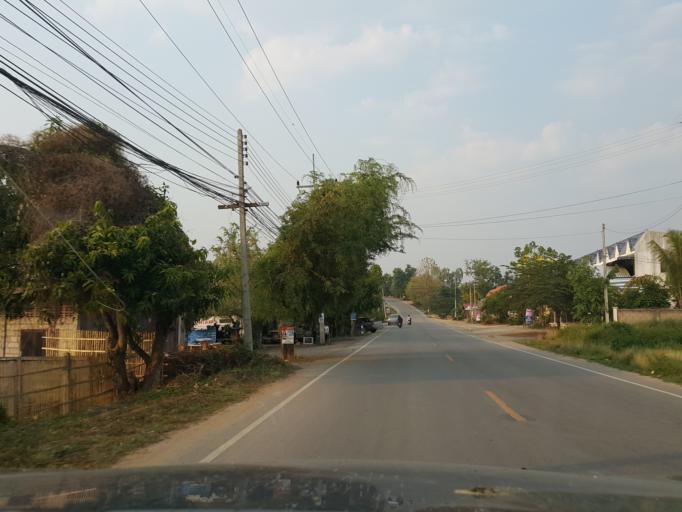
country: TH
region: Lamphun
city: Li
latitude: 17.8093
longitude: 98.9575
